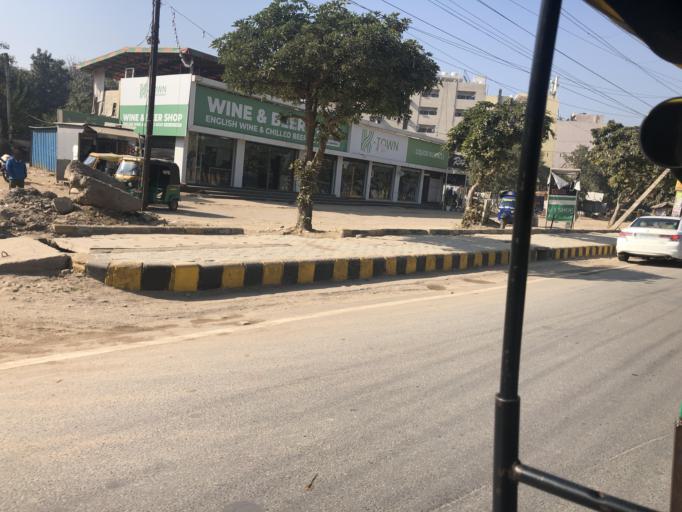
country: IN
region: Haryana
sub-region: Gurgaon
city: Gurgaon
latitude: 28.4485
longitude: 77.0732
